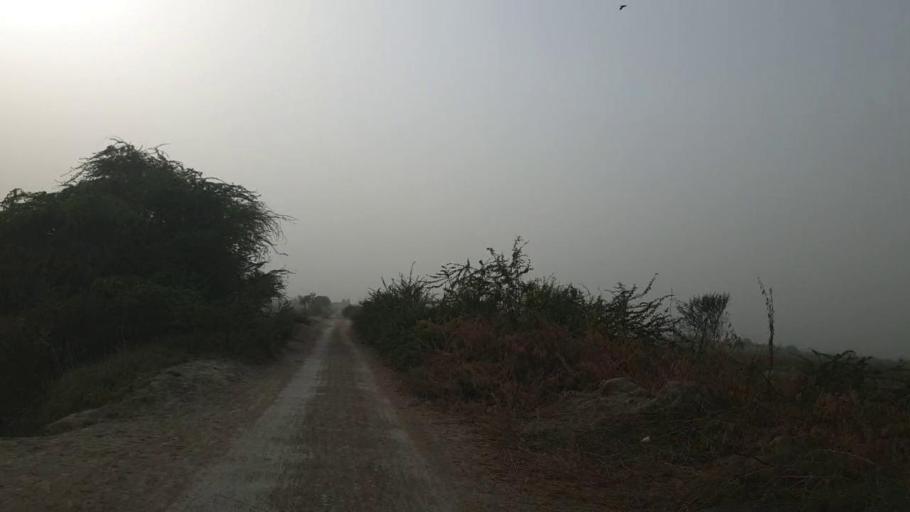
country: PK
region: Sindh
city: Kunri
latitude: 25.0669
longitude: 69.4519
